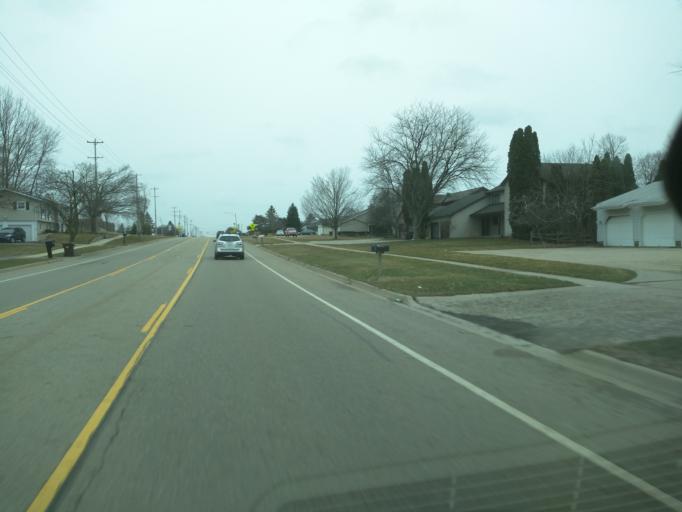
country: US
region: Michigan
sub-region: Eaton County
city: Waverly
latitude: 42.7491
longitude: -84.6225
